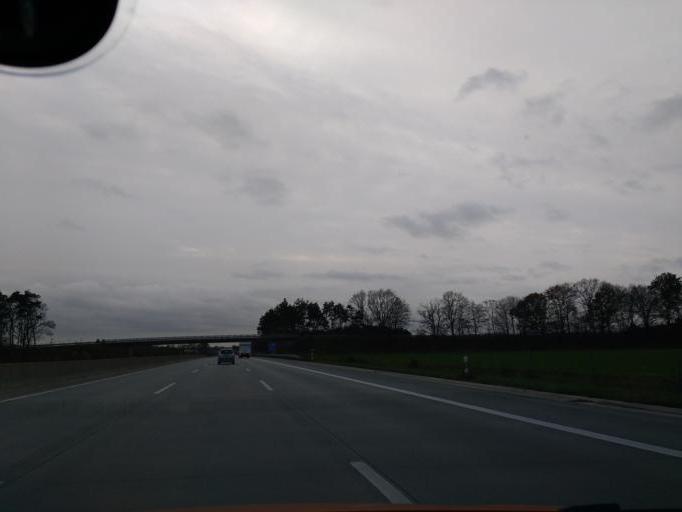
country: DE
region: Lower Saxony
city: Gross Meckelsen
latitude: 53.2655
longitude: 9.4461
